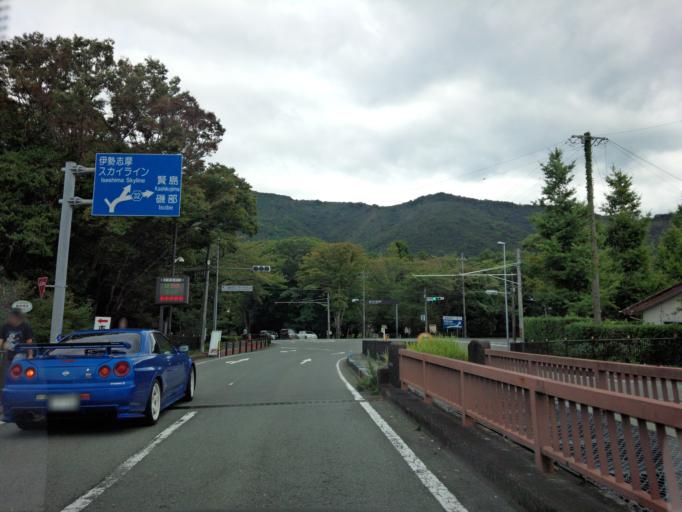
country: JP
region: Mie
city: Ise
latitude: 34.4650
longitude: 136.7254
